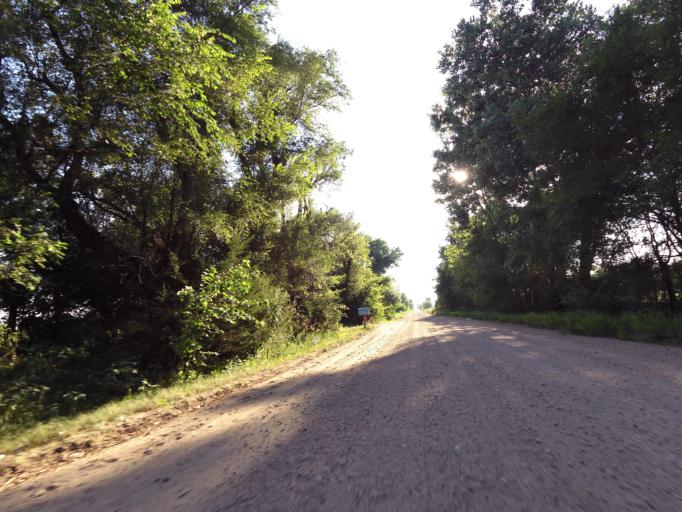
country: US
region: Kansas
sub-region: McPherson County
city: Inman
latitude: 38.1883
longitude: -97.8656
